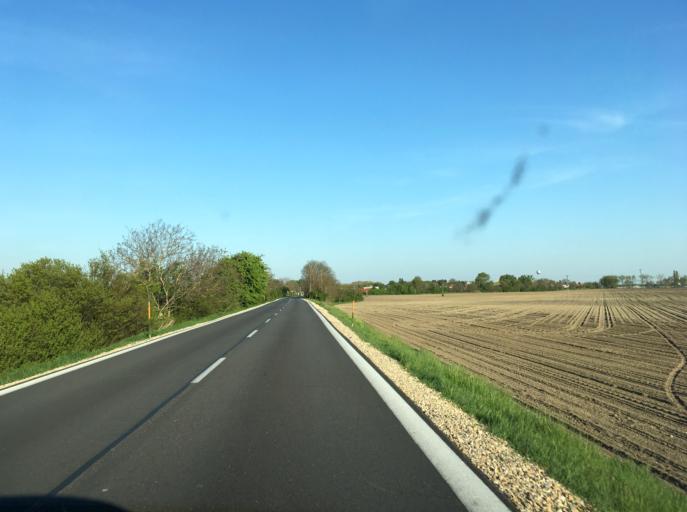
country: AT
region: Burgenland
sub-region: Politischer Bezirk Neusiedl am See
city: Deutsch Jahrndorf
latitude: 48.0597
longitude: 17.1322
